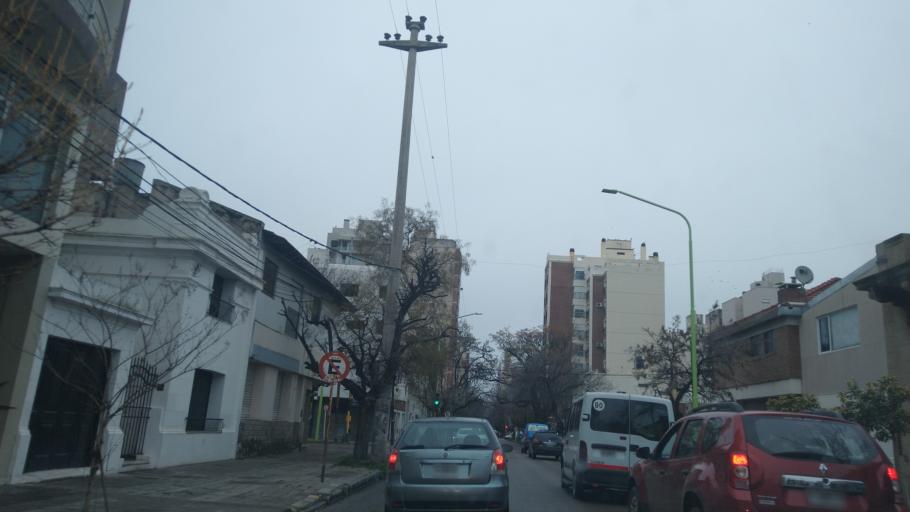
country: AR
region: Buenos Aires
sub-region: Partido de Bahia Blanca
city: Bahia Blanca
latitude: -38.7124
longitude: -62.2638
